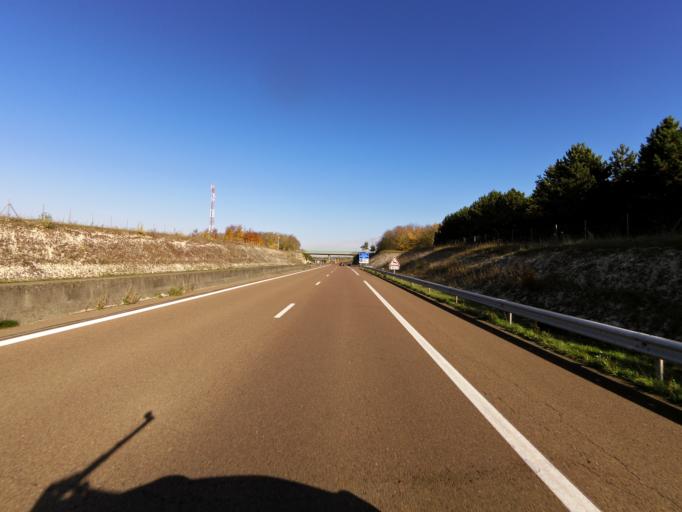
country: FR
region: Champagne-Ardenne
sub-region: Departement de la Marne
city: Compertrix
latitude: 48.8767
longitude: 4.2897
